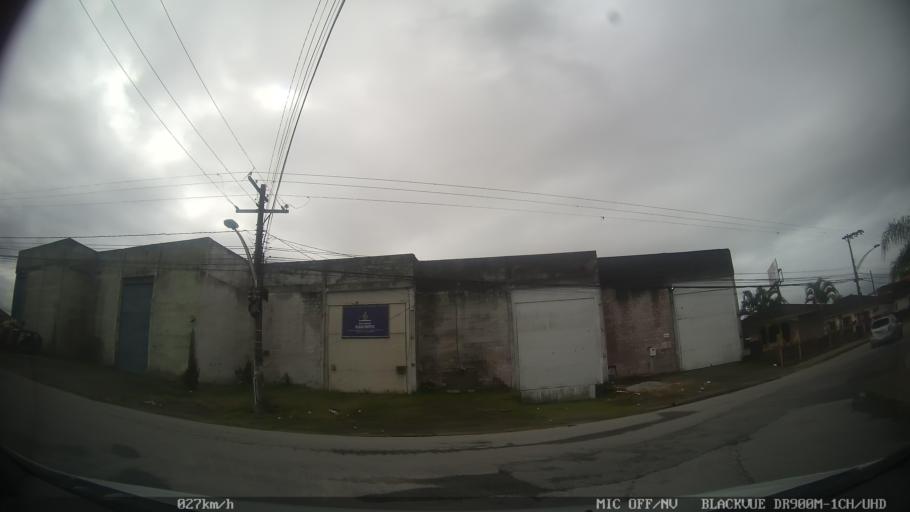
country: BR
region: Santa Catarina
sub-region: Biguacu
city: Biguacu
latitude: -27.5132
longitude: -48.6420
